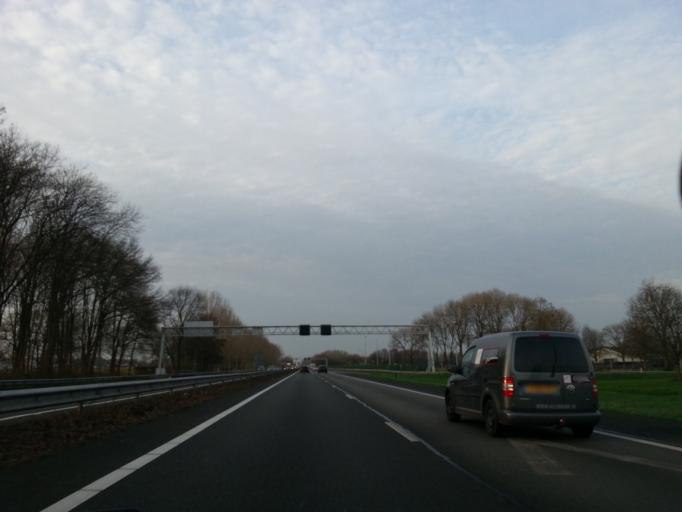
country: NL
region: Gelderland
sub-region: Gemeente Zevenaar
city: Zevenaar
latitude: 51.9376
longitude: 6.0923
